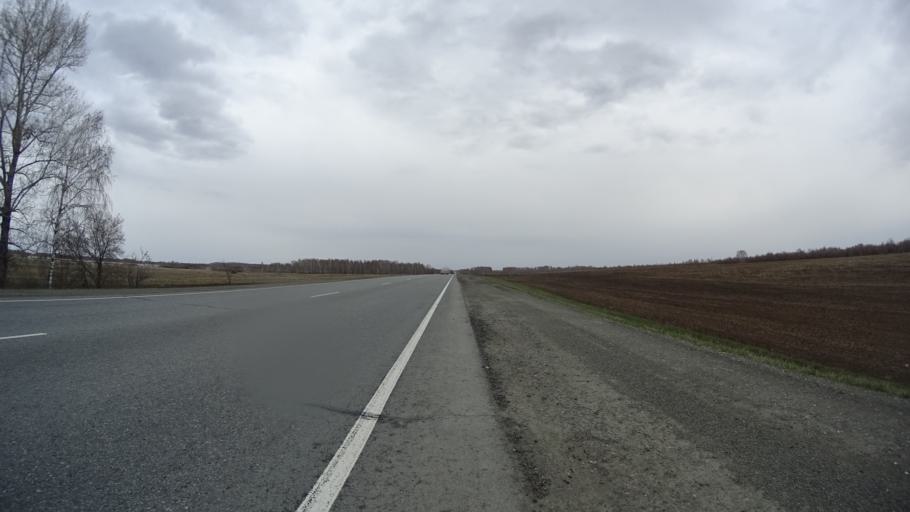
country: RU
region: Chelyabinsk
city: Krasnogorskiy
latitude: 54.6645
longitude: 61.2532
